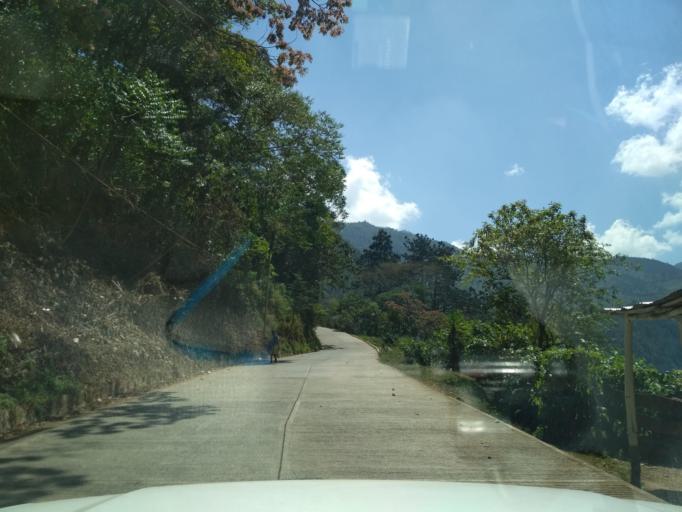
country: MX
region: Veracruz
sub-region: Tlilapan
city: Tonalixco
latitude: 18.7767
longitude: -97.0820
